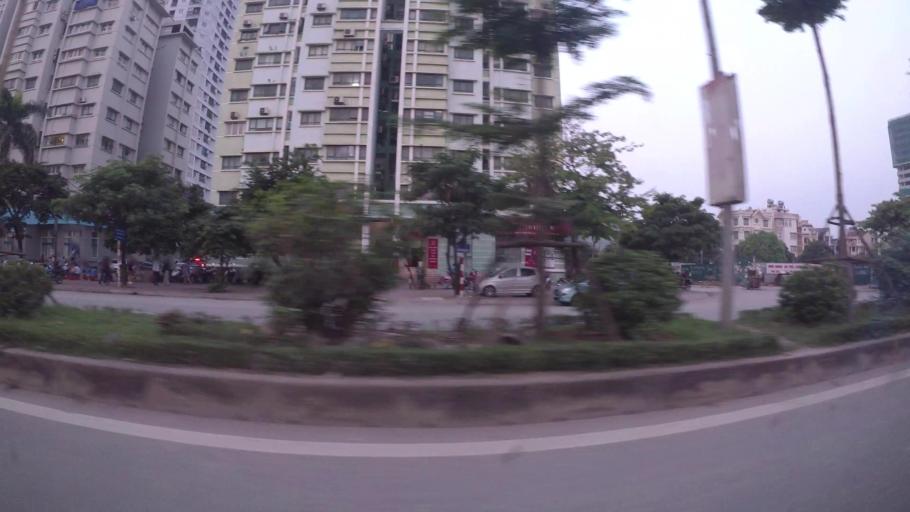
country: VN
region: Ha Noi
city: Tay Ho
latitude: 21.0677
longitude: 105.7867
